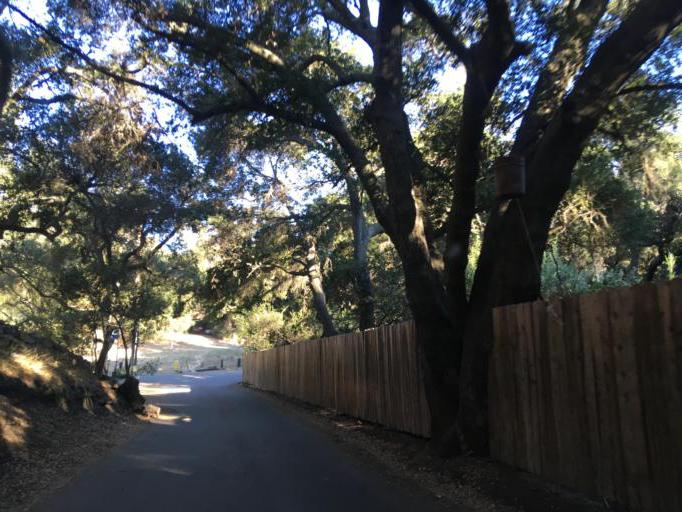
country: US
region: California
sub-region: Los Angeles County
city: Westlake Village
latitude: 34.0913
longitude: -118.8185
